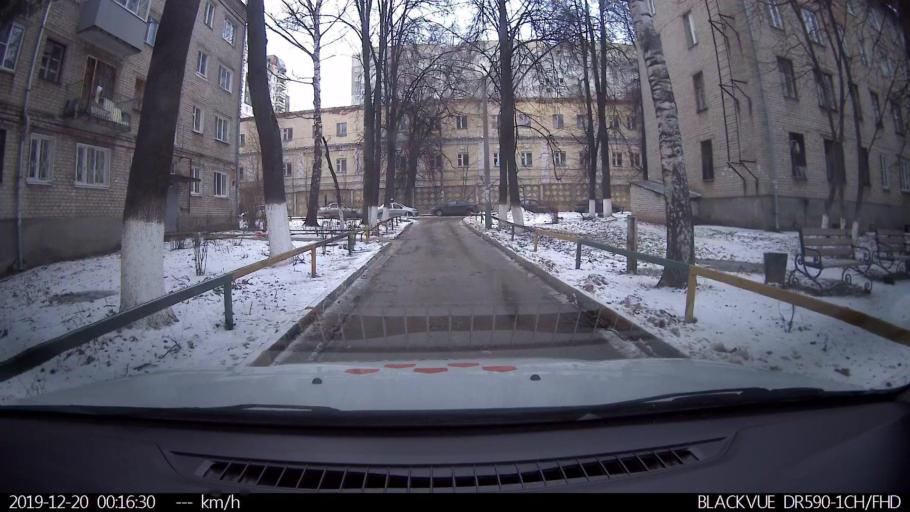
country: RU
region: Jaroslavl
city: Petrovsk
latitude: 56.9541
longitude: 39.4028
